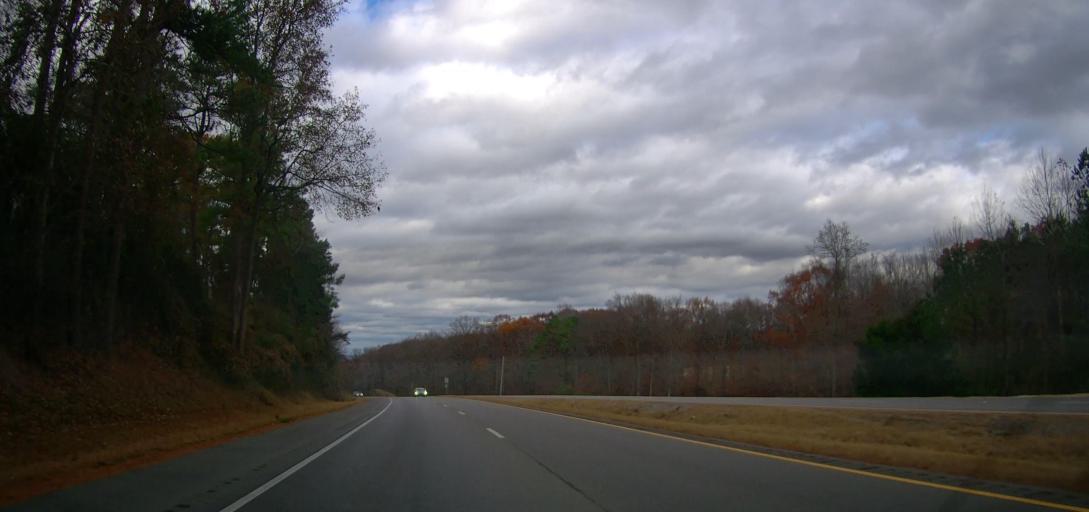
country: US
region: Alabama
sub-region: Morgan County
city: Falkville
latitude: 34.3049
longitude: -86.9967
